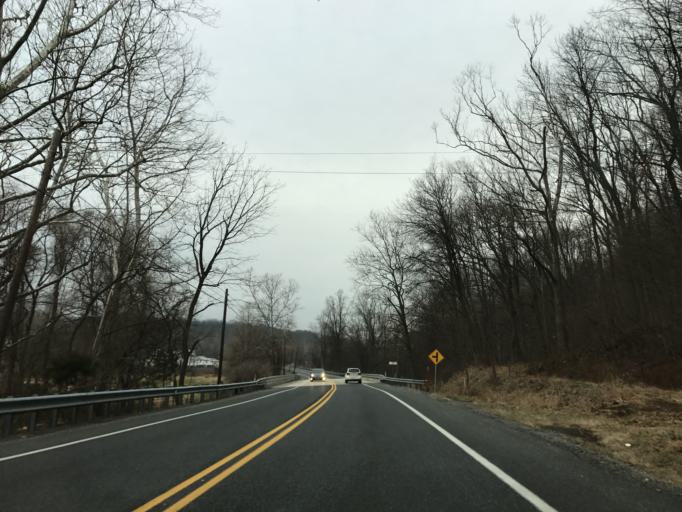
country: US
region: Pennsylvania
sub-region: Adams County
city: Carroll Valley
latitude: 39.7310
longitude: -77.3654
